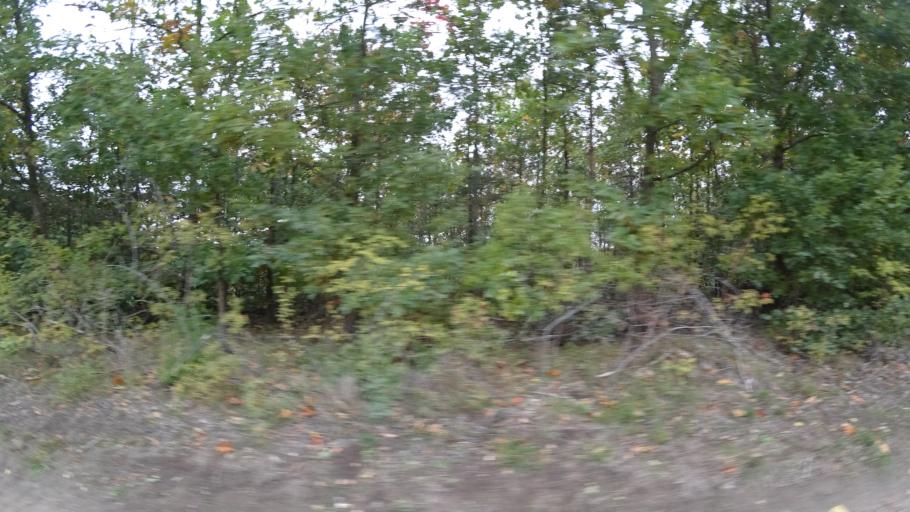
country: SE
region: Skane
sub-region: Kavlinge Kommun
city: Hofterup
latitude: 55.8232
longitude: 12.9629
